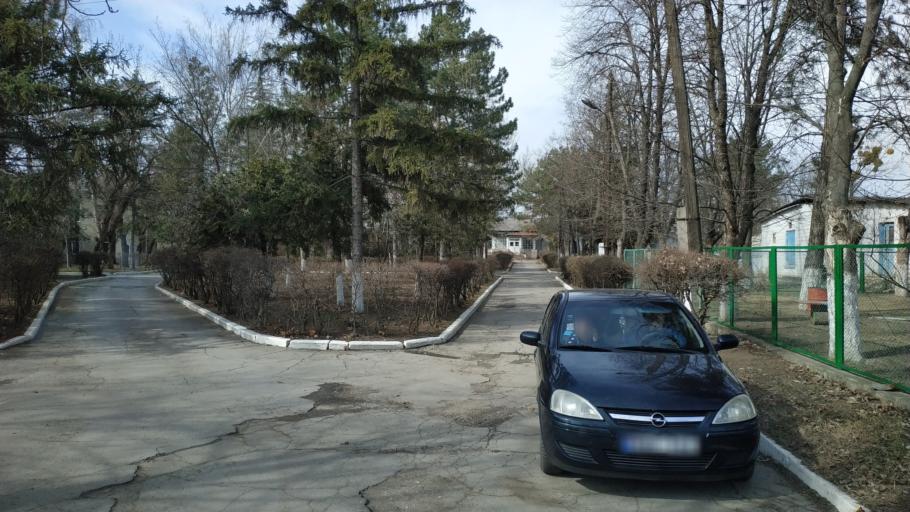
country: MD
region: Chisinau
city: Vatra
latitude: 47.0961
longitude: 28.6774
